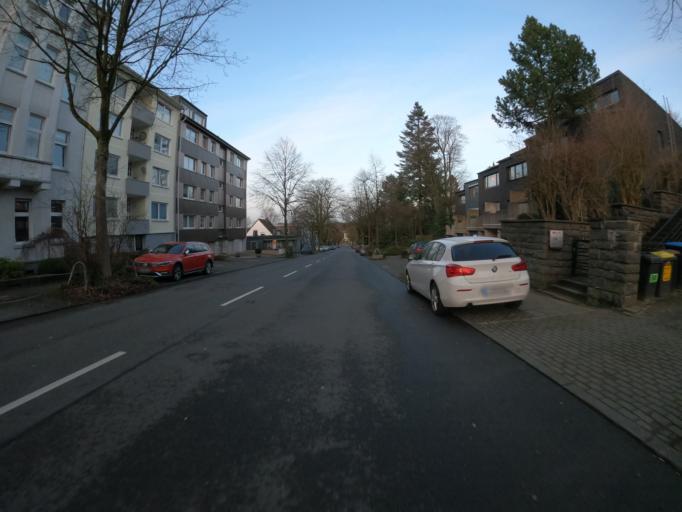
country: DE
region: North Rhine-Westphalia
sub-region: Regierungsbezirk Dusseldorf
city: Wuppertal
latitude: 51.2369
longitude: 7.1557
